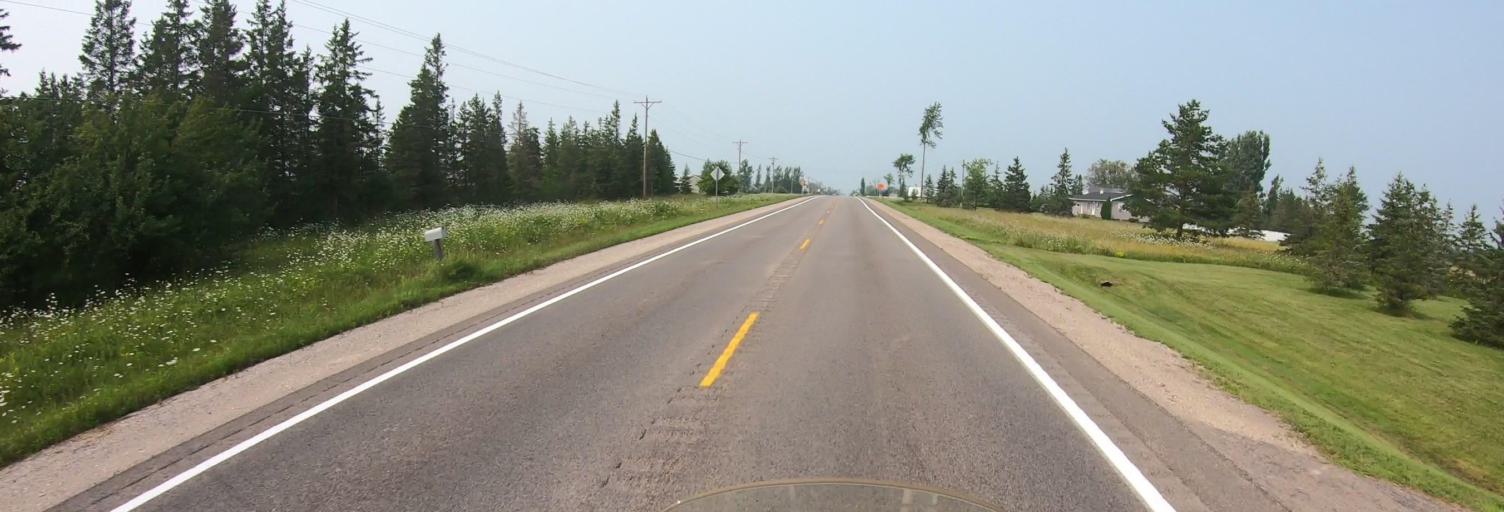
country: US
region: Michigan
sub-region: Chippewa County
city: Sault Ste. Marie
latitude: 46.1459
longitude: -84.3634
